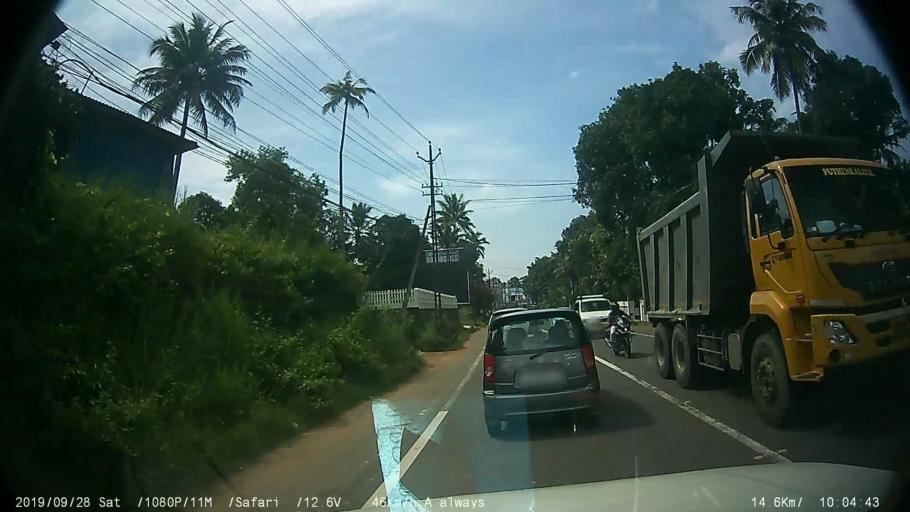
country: IN
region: Kerala
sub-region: Kottayam
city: Kottayam
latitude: 9.6415
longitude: 76.5443
